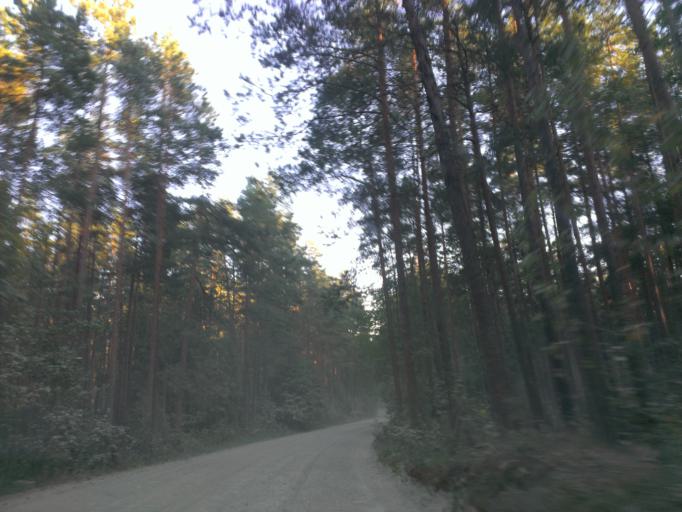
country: LV
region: Garkalne
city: Garkalne
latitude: 57.0628
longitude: 24.4109
